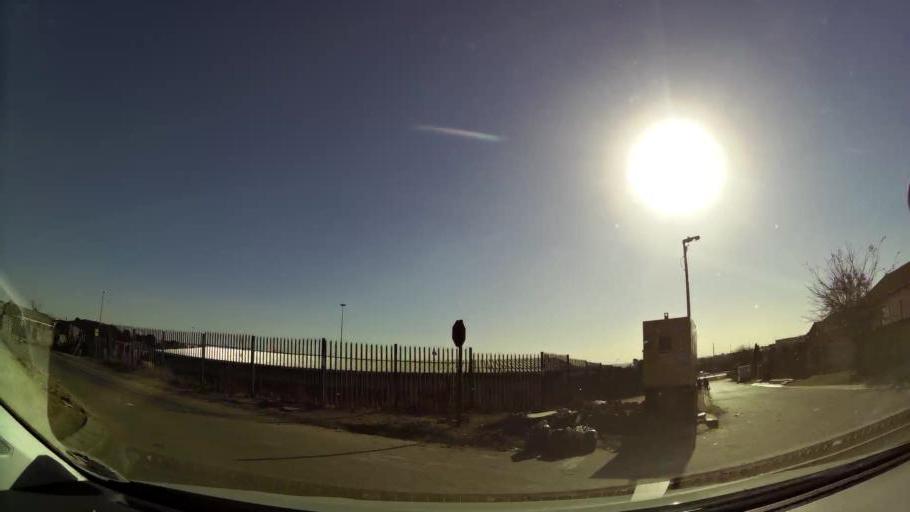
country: ZA
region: Gauteng
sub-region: Ekurhuleni Metropolitan Municipality
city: Tembisa
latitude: -26.0186
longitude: 28.2181
